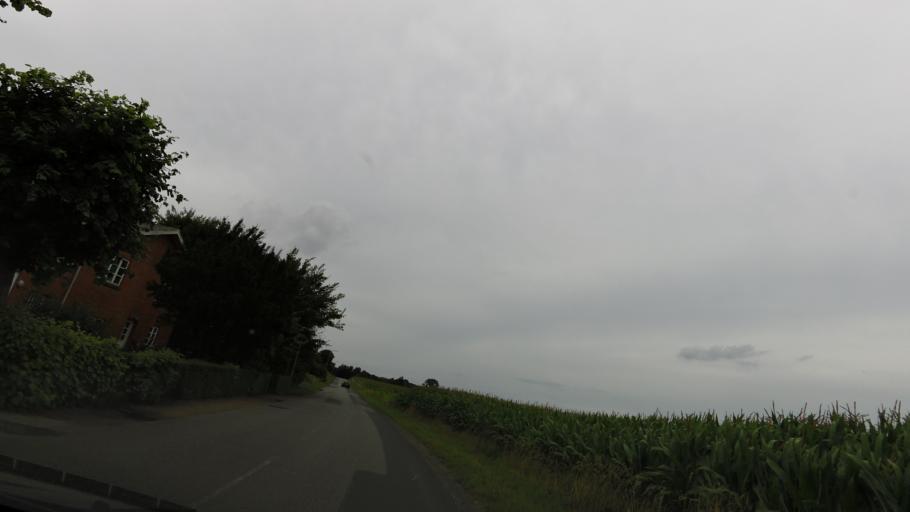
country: DK
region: South Denmark
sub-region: Nordfyns Kommune
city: Otterup
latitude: 55.5761
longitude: 10.3951
